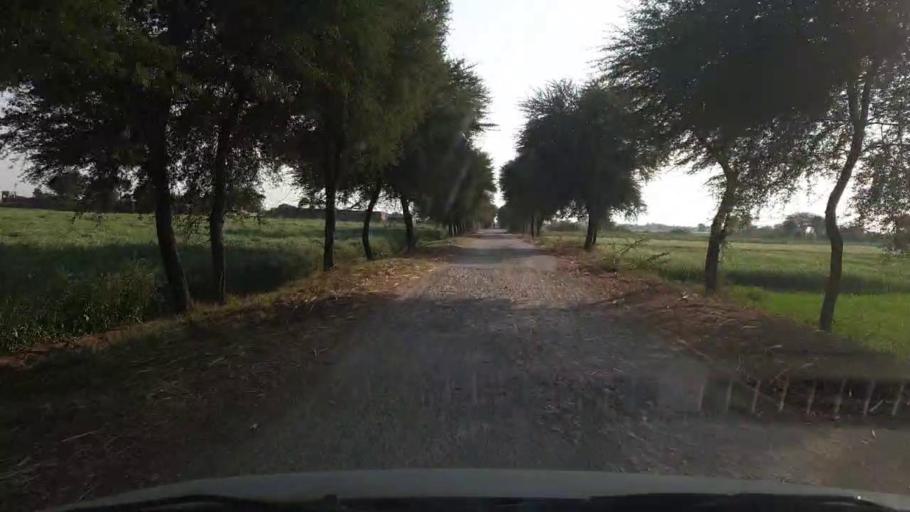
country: PK
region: Sindh
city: Samaro
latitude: 25.2705
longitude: 69.3624
